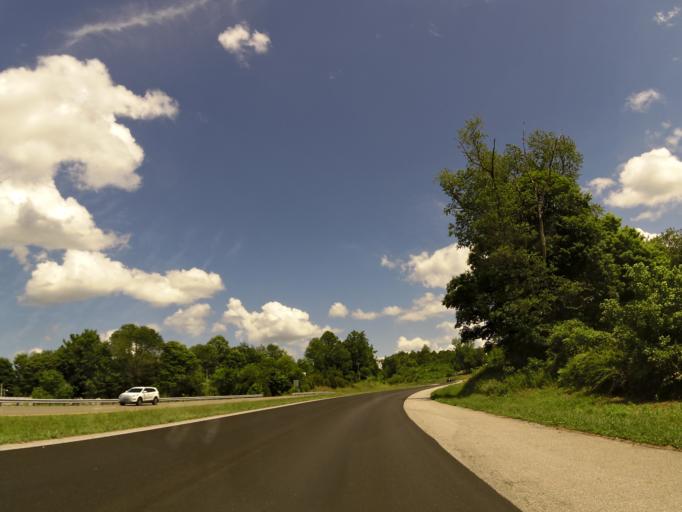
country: US
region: Virginia
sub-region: Lee County
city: Jonesville
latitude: 36.6989
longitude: -83.2559
